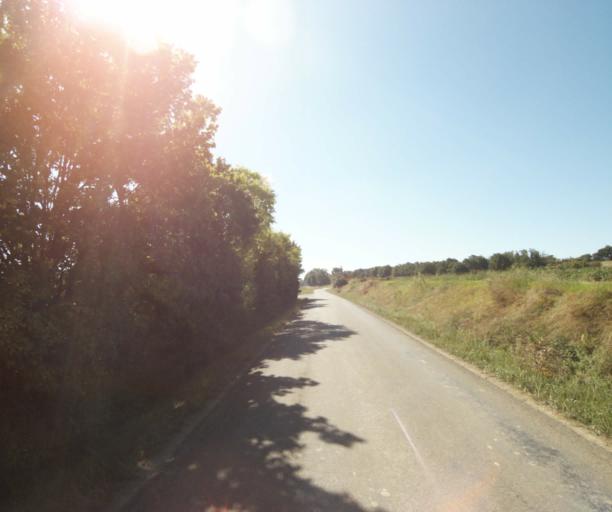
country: FR
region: Midi-Pyrenees
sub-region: Departement du Tarn-et-Garonne
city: Verdun-sur-Garonne
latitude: 43.8391
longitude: 1.2021
